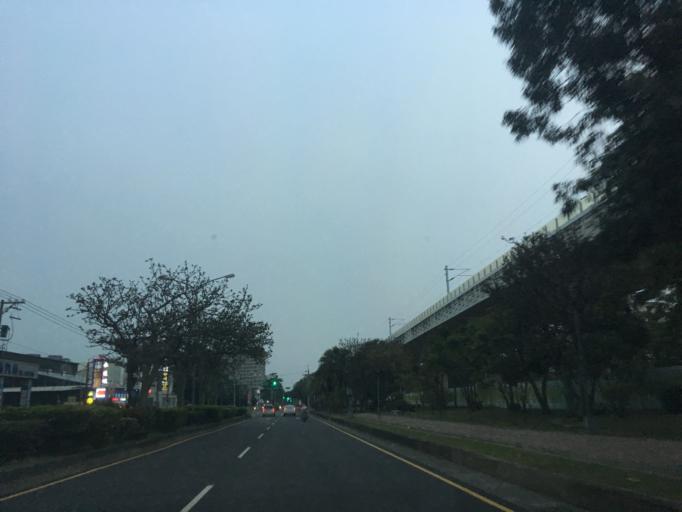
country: TW
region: Taiwan
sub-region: Taichung City
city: Taichung
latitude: 24.1581
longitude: 120.6996
